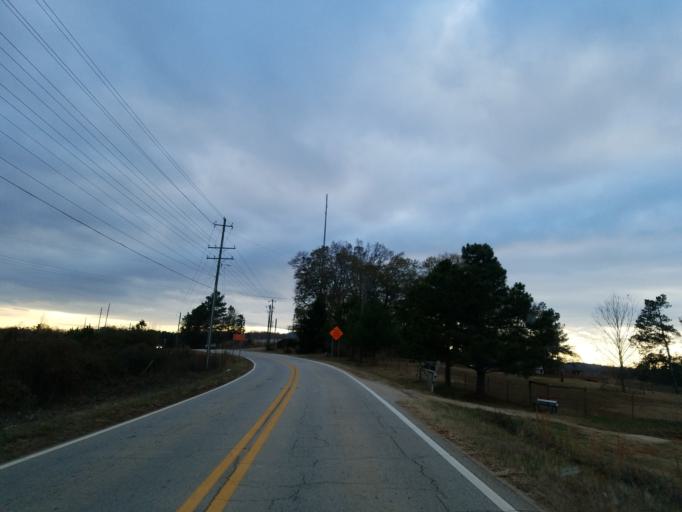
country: US
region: Georgia
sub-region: Dawson County
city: Dawsonville
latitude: 34.3715
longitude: -84.0381
